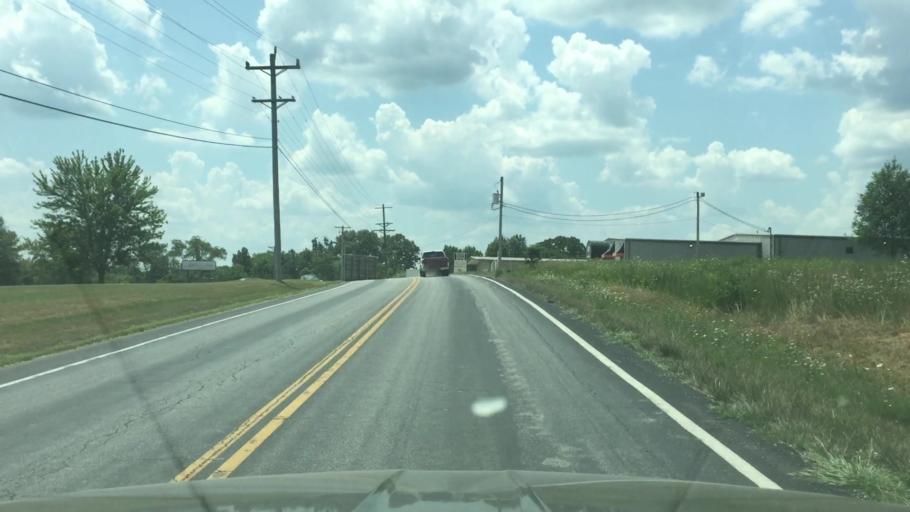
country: US
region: Missouri
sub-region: Camden County
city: Osage Beach
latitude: 38.1419
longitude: -92.5914
